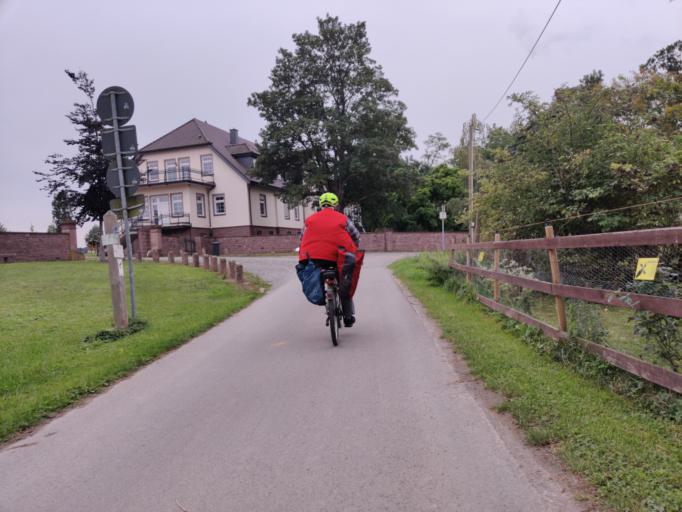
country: DE
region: Lower Saxony
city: Polle
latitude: 51.8989
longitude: 9.4155
